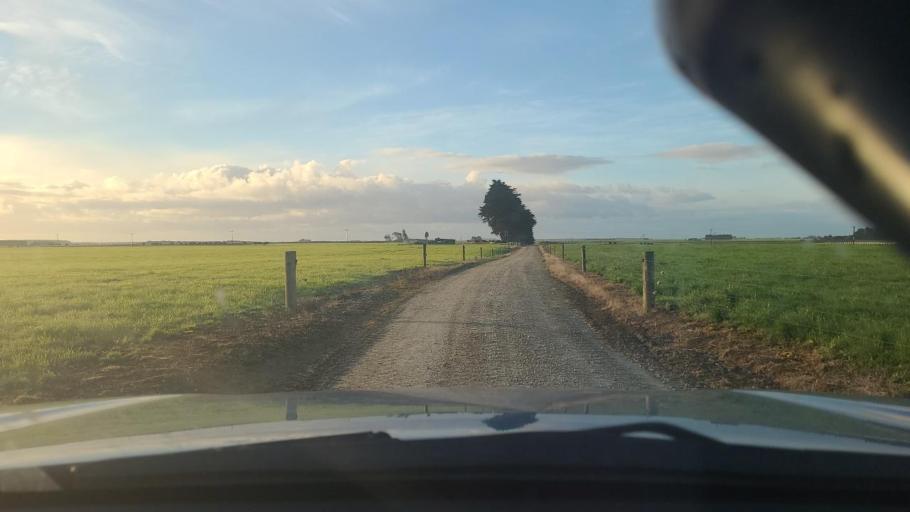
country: NZ
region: Southland
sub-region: Invercargill City
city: Invercargill
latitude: -46.4710
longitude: 168.6760
